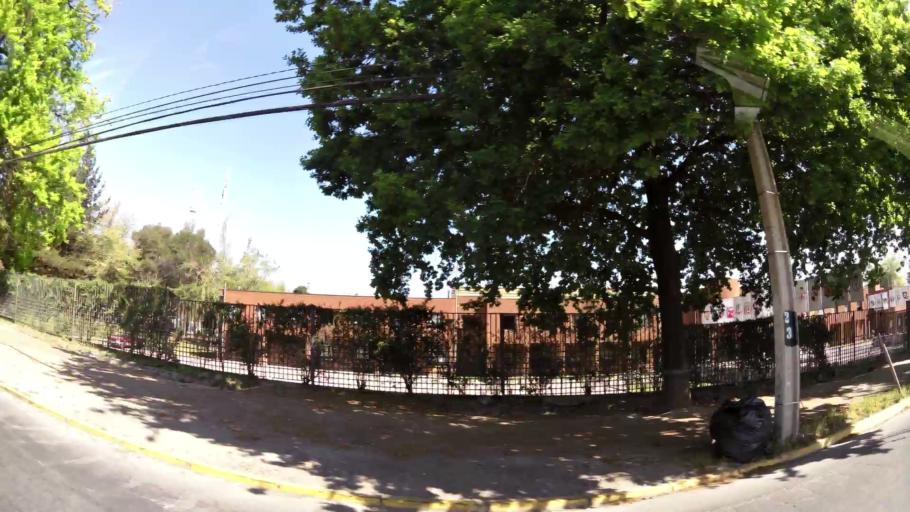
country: CL
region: Santiago Metropolitan
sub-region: Provincia de Santiago
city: Villa Presidente Frei, Nunoa, Santiago, Chile
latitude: -33.4919
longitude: -70.5731
